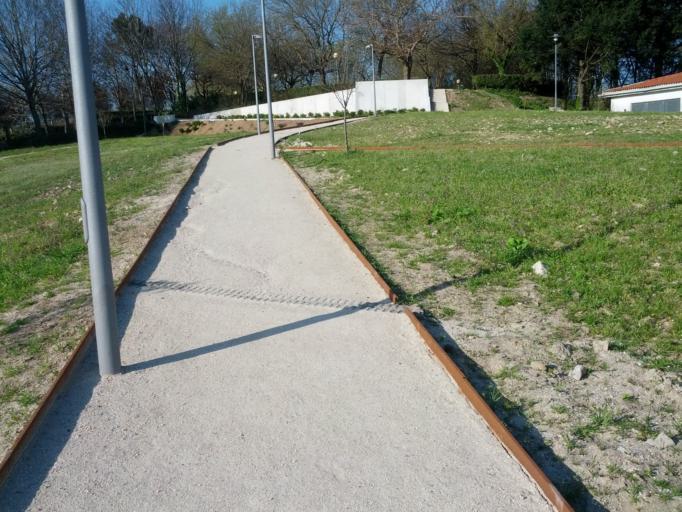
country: ES
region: Galicia
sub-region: Provincia da Coruna
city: Santiago de Compostela
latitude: 42.8853
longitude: -8.5372
